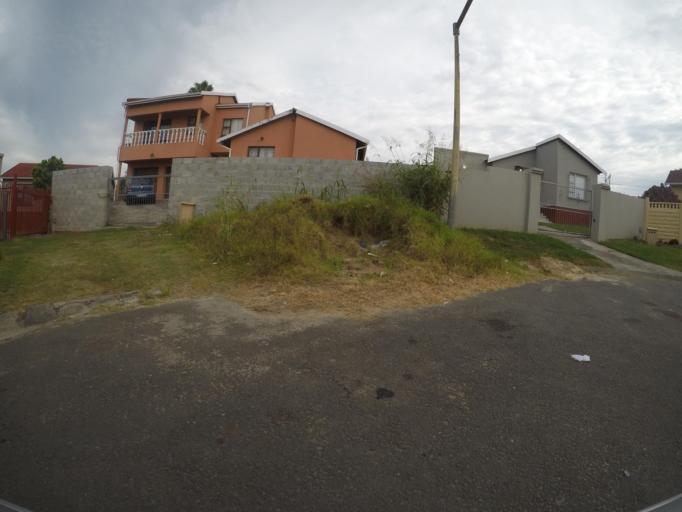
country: ZA
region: Eastern Cape
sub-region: Buffalo City Metropolitan Municipality
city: East London
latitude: -32.9711
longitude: 27.8637
